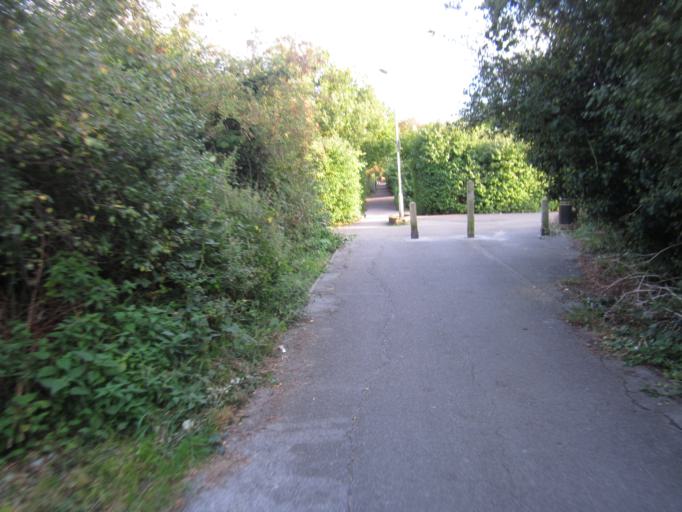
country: GB
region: England
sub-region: Kent
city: Tankerton
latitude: 51.3493
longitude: 1.0436
